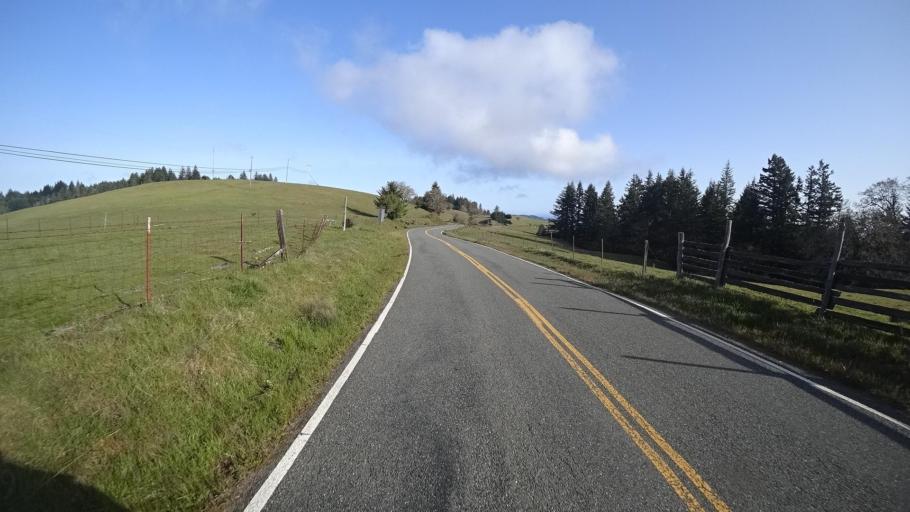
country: US
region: California
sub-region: Humboldt County
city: Blue Lake
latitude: 40.7270
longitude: -123.9450
